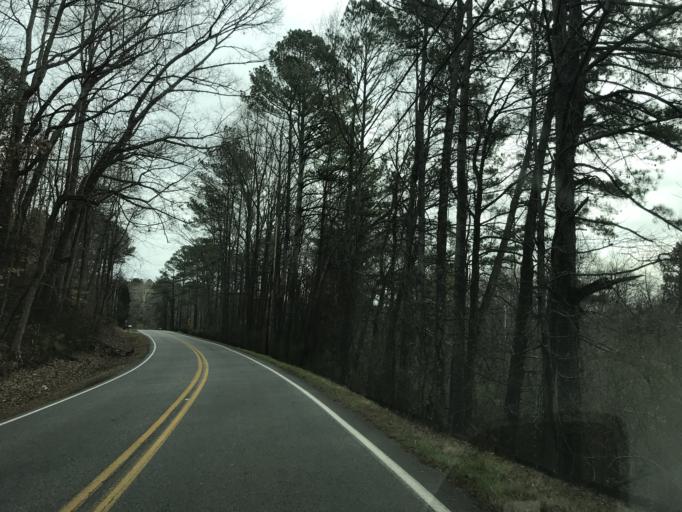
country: US
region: Georgia
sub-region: Cherokee County
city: Canton
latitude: 34.2027
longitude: -84.3914
